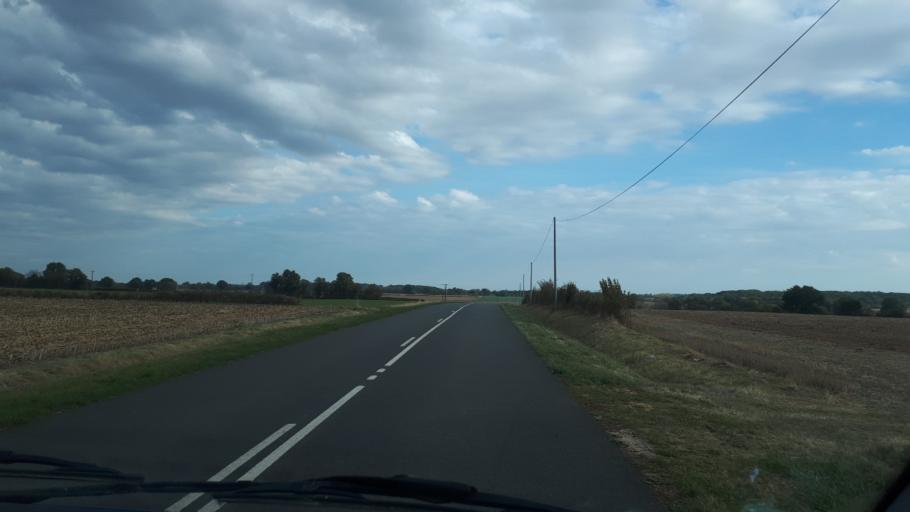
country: FR
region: Centre
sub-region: Departement du Loir-et-Cher
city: Mondoubleau
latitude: 48.0081
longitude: 0.9191
